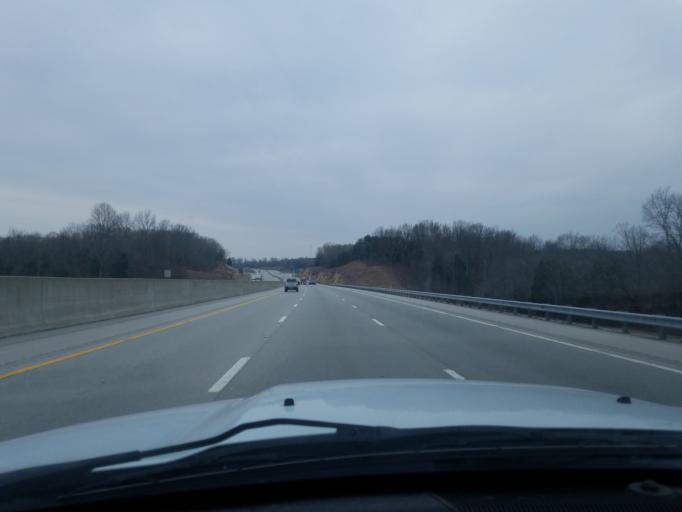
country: US
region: Kentucky
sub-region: Barren County
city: Cave City
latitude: 37.1038
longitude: -86.0464
